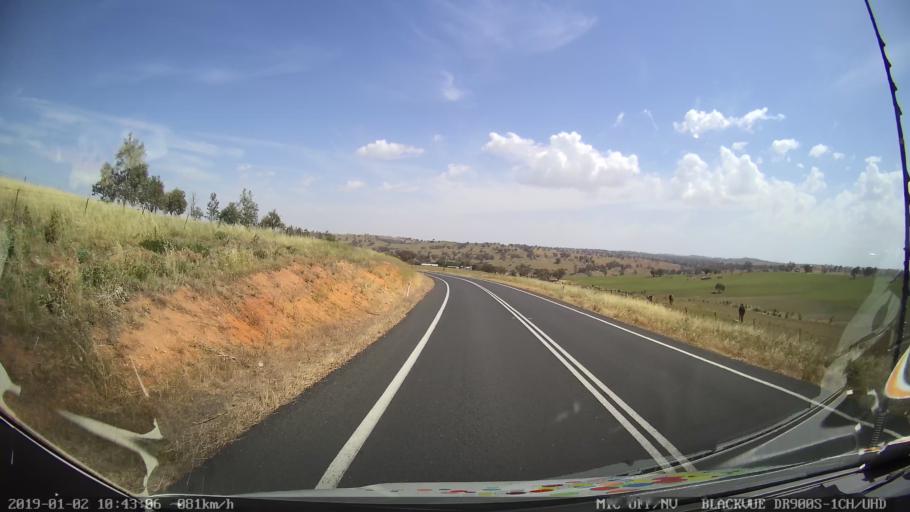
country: AU
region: New South Wales
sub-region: Cootamundra
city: Cootamundra
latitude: -34.7764
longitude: 148.3058
